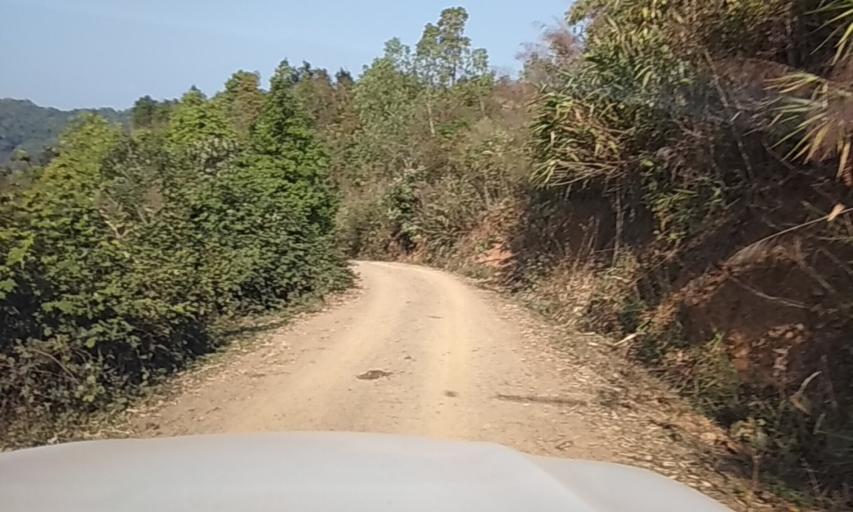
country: LA
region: Phongsali
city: Phongsali
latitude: 21.6938
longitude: 102.0915
